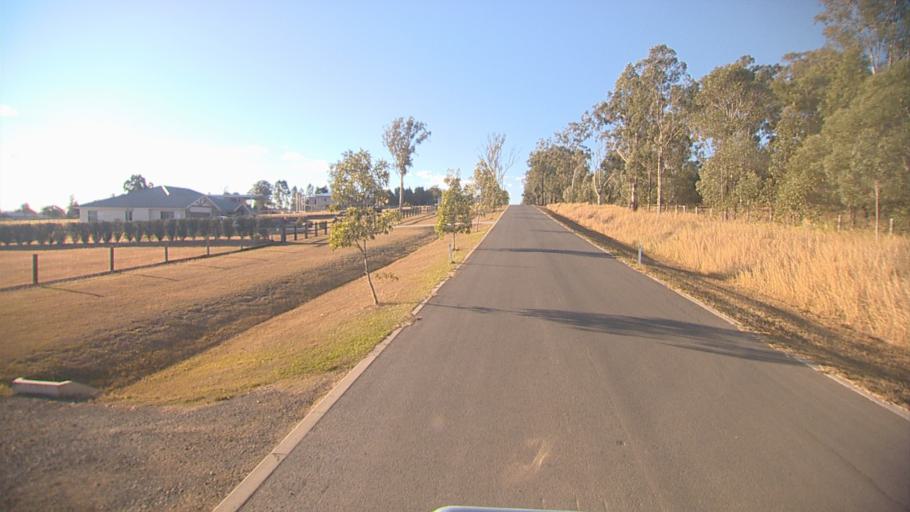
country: AU
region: Queensland
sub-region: Logan
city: Cedar Vale
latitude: -27.8740
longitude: 152.9741
